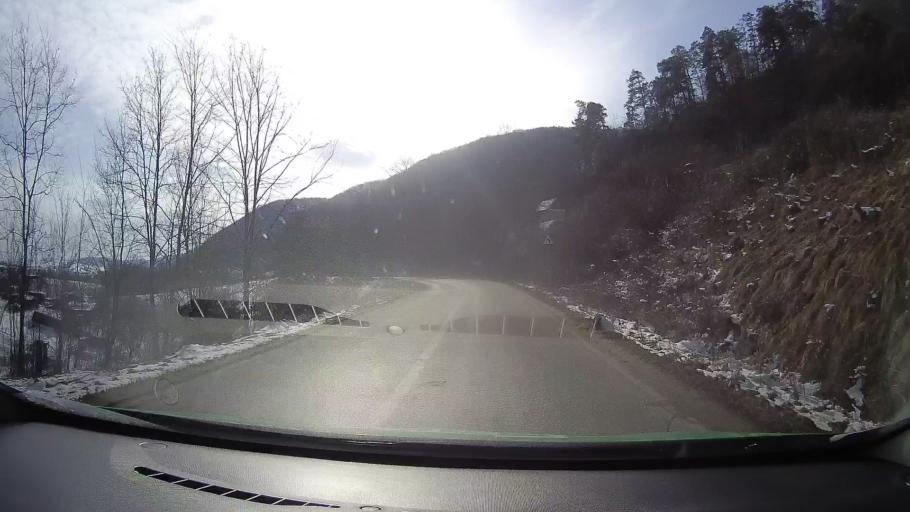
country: RO
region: Mures
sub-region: Municipiul Sighisoara
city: Sighisoara
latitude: 46.1974
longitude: 24.7662
